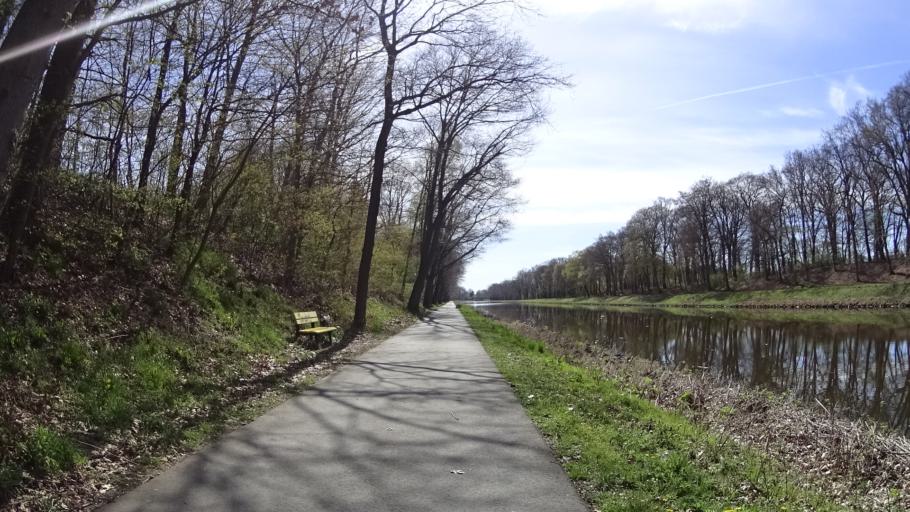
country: DE
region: Lower Saxony
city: Lingen
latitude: 52.5346
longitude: 7.3010
